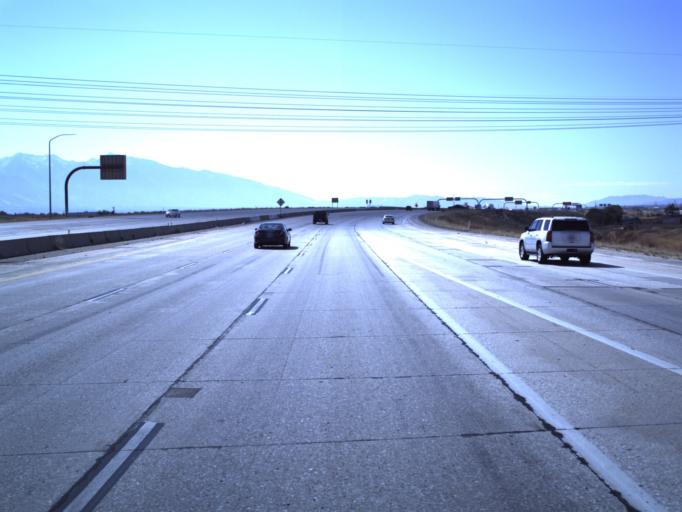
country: US
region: Utah
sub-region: Salt Lake County
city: Salt Lake City
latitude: 40.7564
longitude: -111.9498
